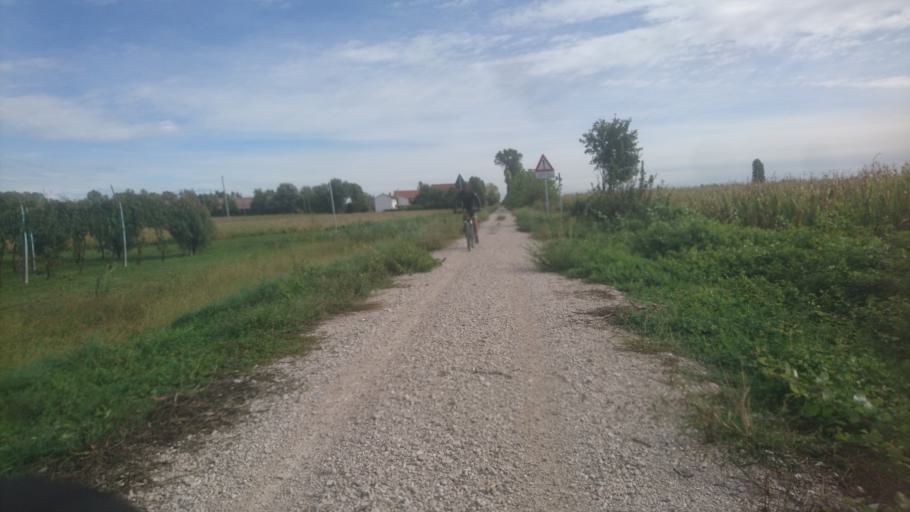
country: IT
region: Veneto
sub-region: Provincia di Vicenza
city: Montegalda
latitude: 45.4671
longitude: 11.6557
